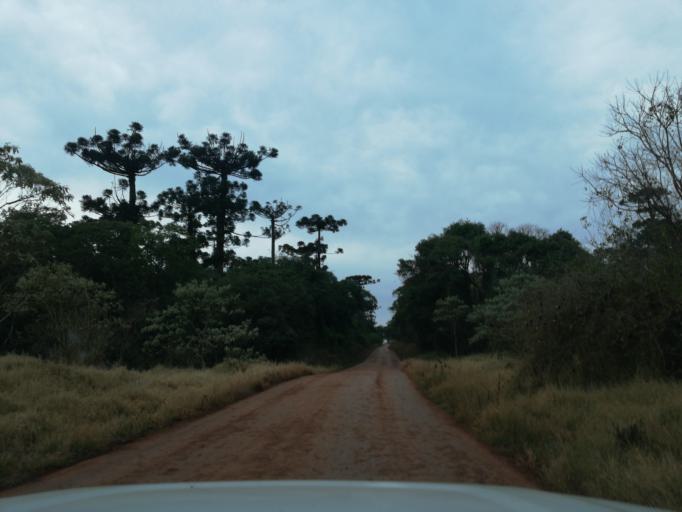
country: AR
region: Misiones
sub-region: Departamento de San Pedro
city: San Pedro
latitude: -26.6281
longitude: -54.1015
